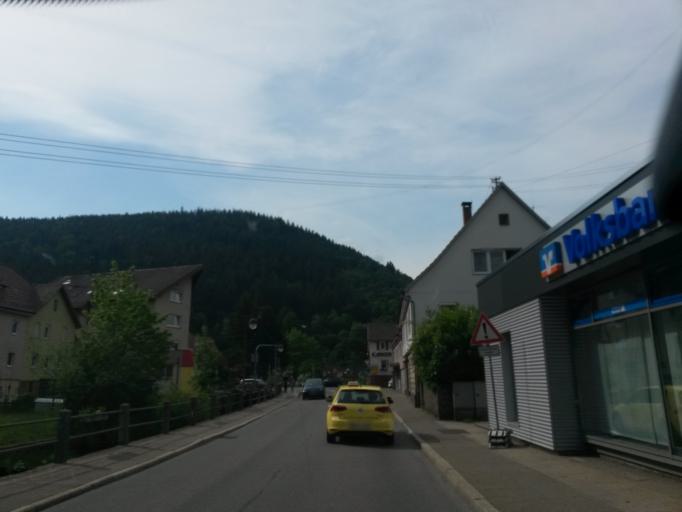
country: DE
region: Baden-Wuerttemberg
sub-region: Karlsruhe Region
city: Hofen an der Enz
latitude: 48.7749
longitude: 8.5771
